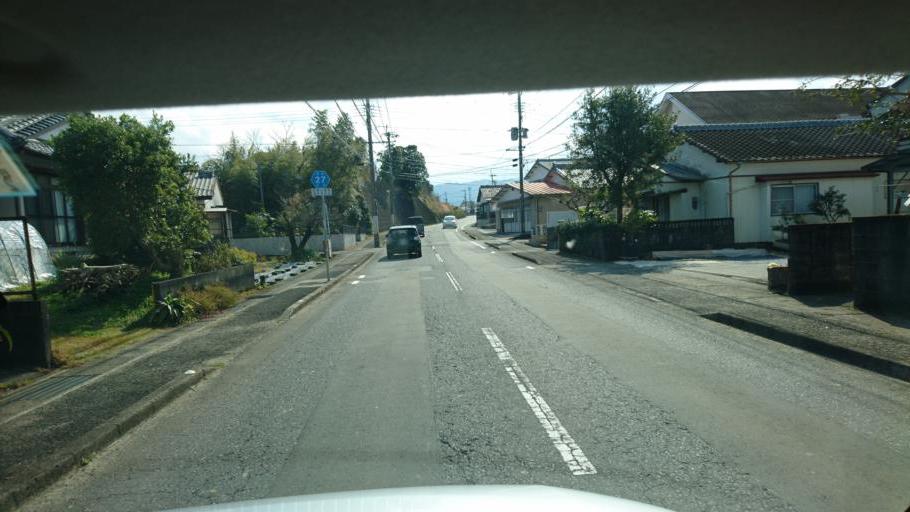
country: JP
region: Miyazaki
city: Miyazaki-shi
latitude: 31.8455
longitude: 131.3938
